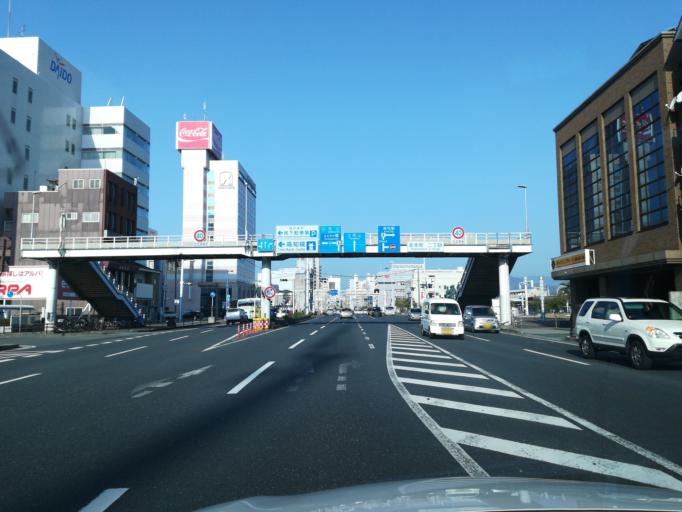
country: JP
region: Kochi
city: Kochi-shi
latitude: 33.5661
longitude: 133.5447
